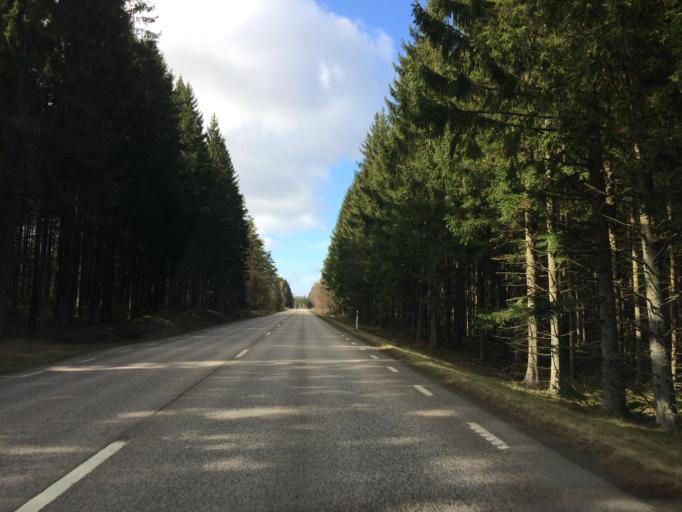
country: SE
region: Halland
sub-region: Laholms Kommun
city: Knared
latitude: 56.4918
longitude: 13.4007
